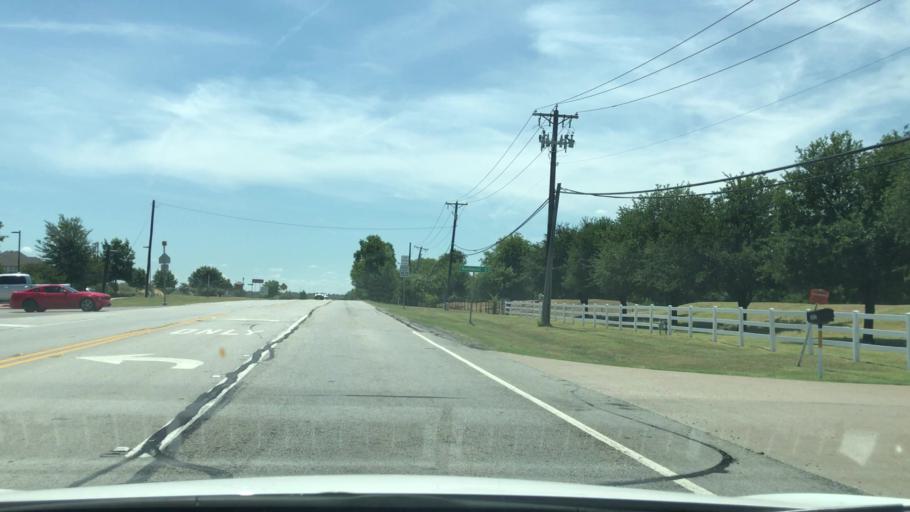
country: US
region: Texas
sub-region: Rockwall County
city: Rockwall
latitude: 32.9644
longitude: -96.4648
